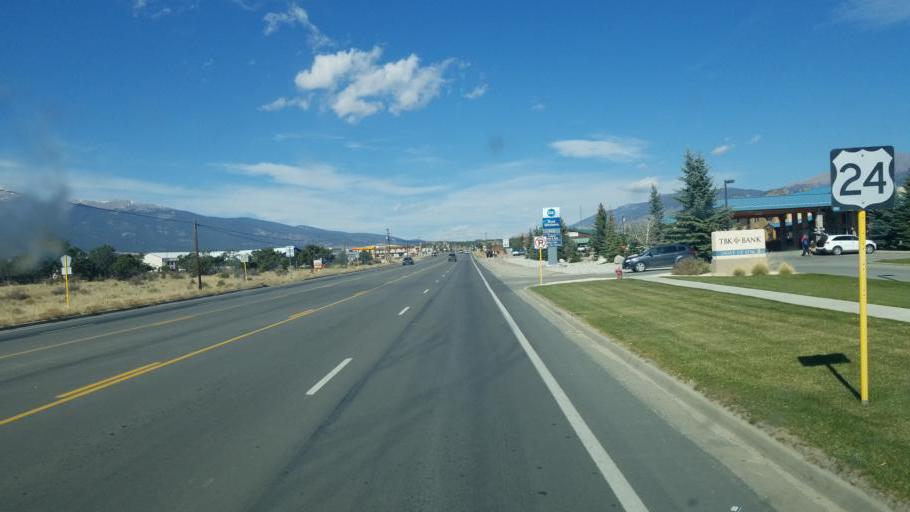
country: US
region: Colorado
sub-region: Chaffee County
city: Buena Vista
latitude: 38.8477
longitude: -106.1360
